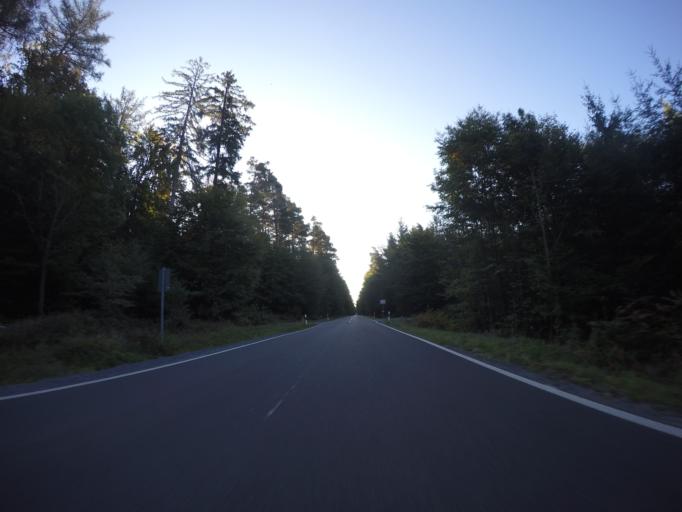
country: DE
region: Bavaria
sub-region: Regierungsbezirk Unterfranken
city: Schollbrunn
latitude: 49.8524
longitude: 9.4374
